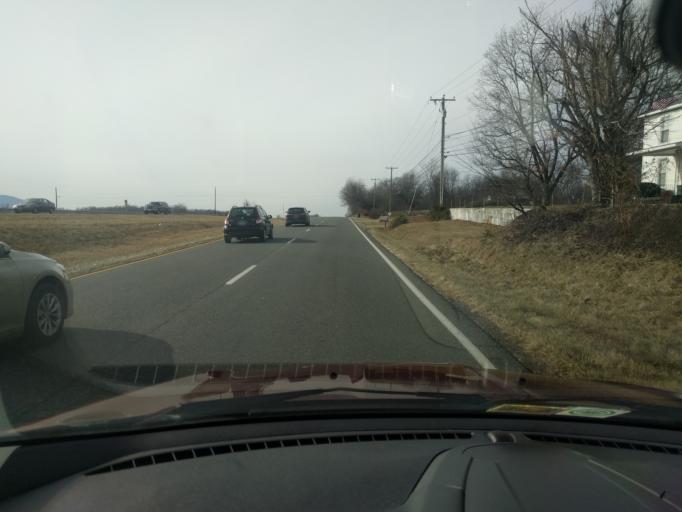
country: US
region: Virginia
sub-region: Augusta County
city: Lyndhurst
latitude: 38.0475
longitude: -78.9765
